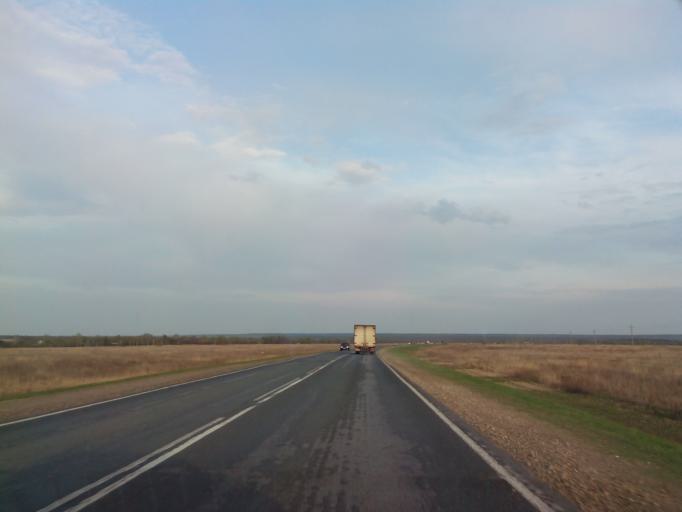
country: RU
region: Rjazan
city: Korablino
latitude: 53.7450
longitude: 39.8785
